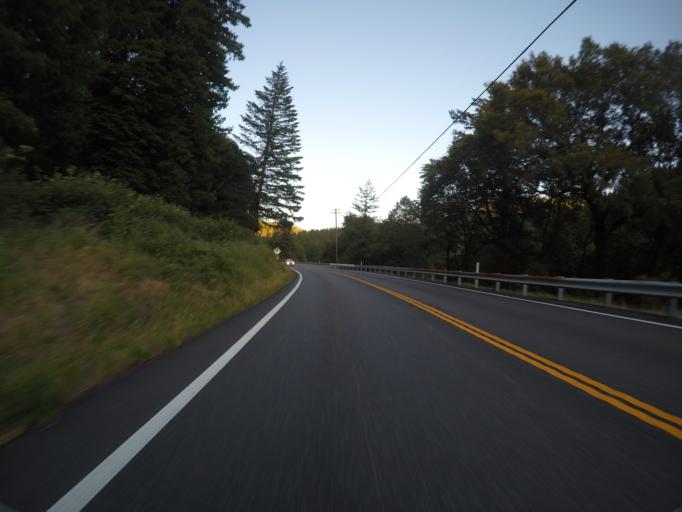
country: US
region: California
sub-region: Humboldt County
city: Redway
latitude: 39.8871
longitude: -123.7468
